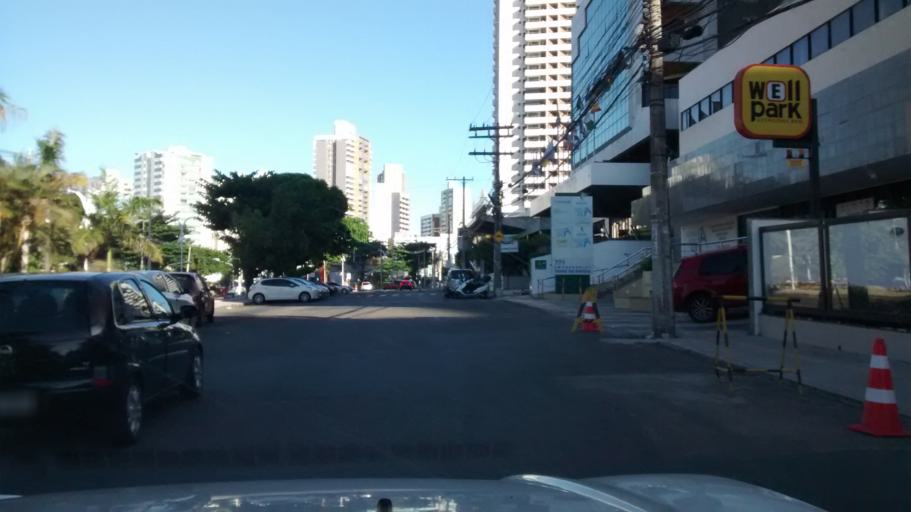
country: BR
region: Bahia
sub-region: Salvador
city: Salvador
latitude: -12.9969
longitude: -38.4657
